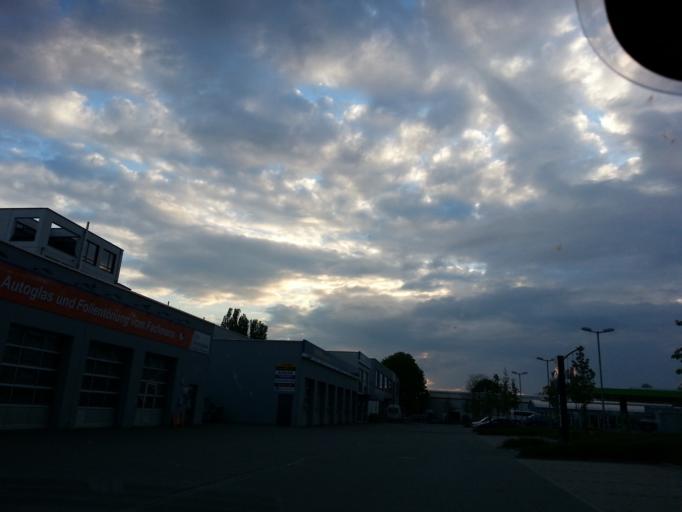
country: DE
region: Berlin
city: Charlottenburg-Nord
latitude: 52.5471
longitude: 13.3111
